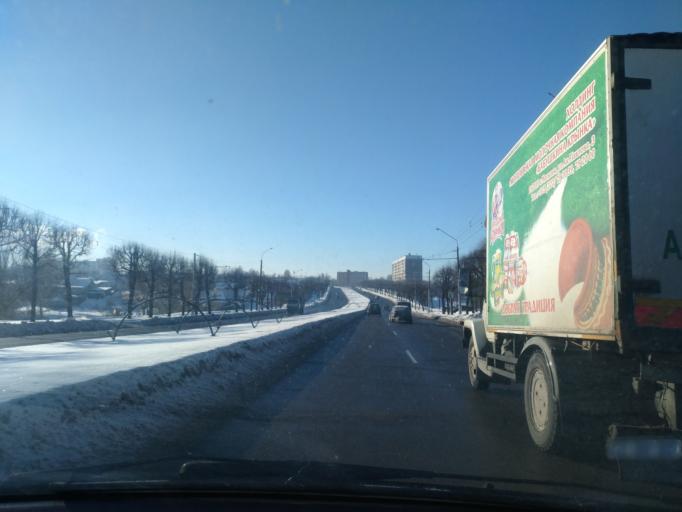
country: BY
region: Mogilev
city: Mahilyow
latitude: 53.9028
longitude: 30.3014
